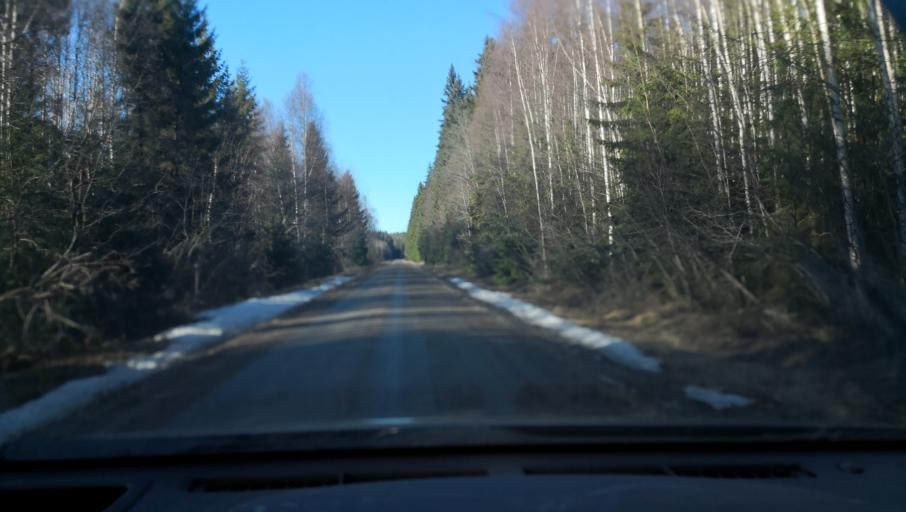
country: SE
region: Vaestmanland
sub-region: Sala Kommun
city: Sala
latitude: 60.1360
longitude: 16.6496
